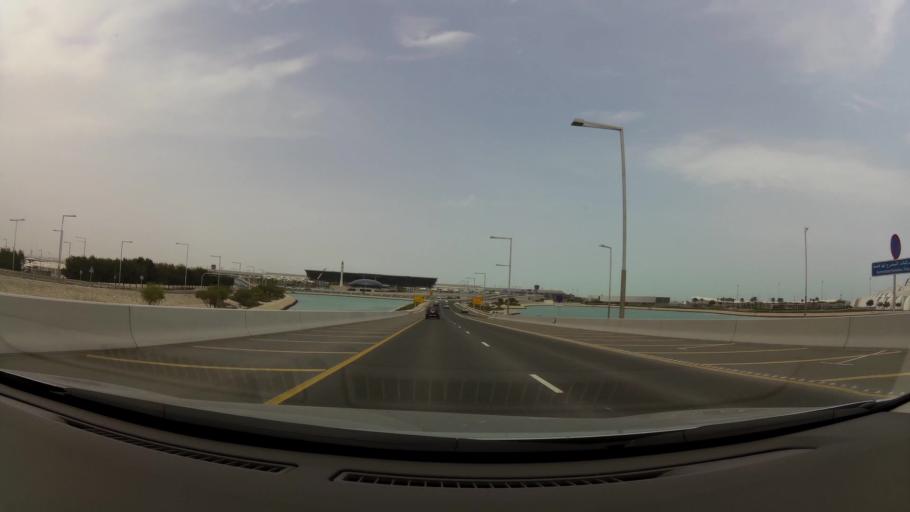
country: QA
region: Al Wakrah
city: Al Wakrah
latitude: 25.2530
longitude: 51.6171
